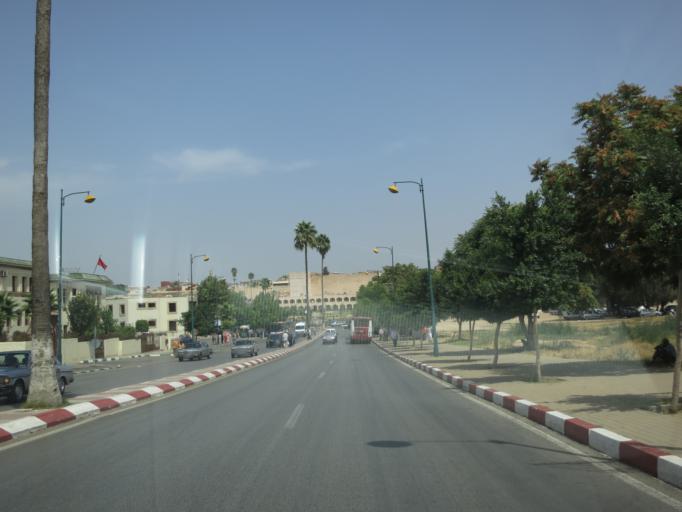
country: MA
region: Meknes-Tafilalet
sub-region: Meknes
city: Meknes
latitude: 33.8888
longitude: -5.5671
